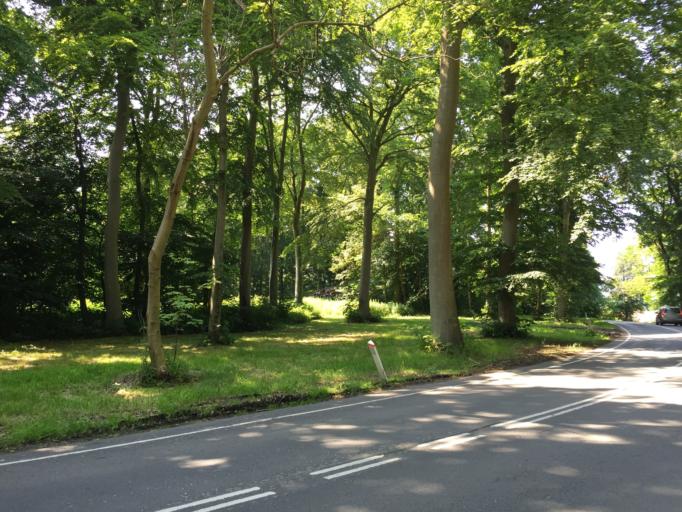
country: DK
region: South Denmark
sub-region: Kerteminde Kommune
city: Kerteminde
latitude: 55.5314
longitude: 10.6510
